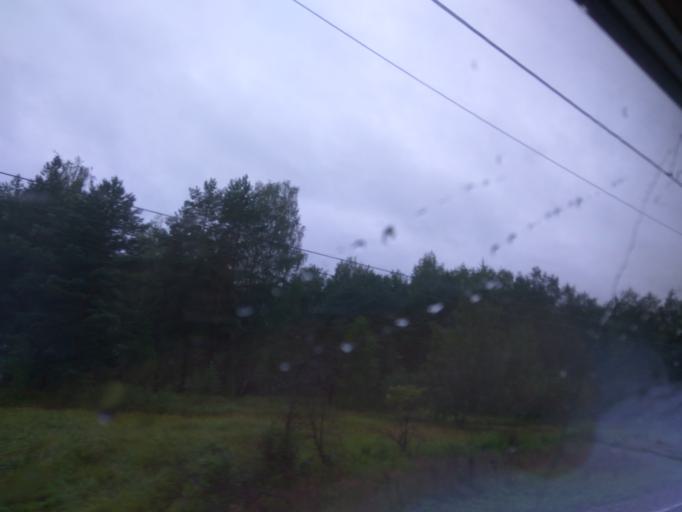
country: RU
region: Moskovskaya
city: Stupino
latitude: 54.8797
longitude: 38.1077
